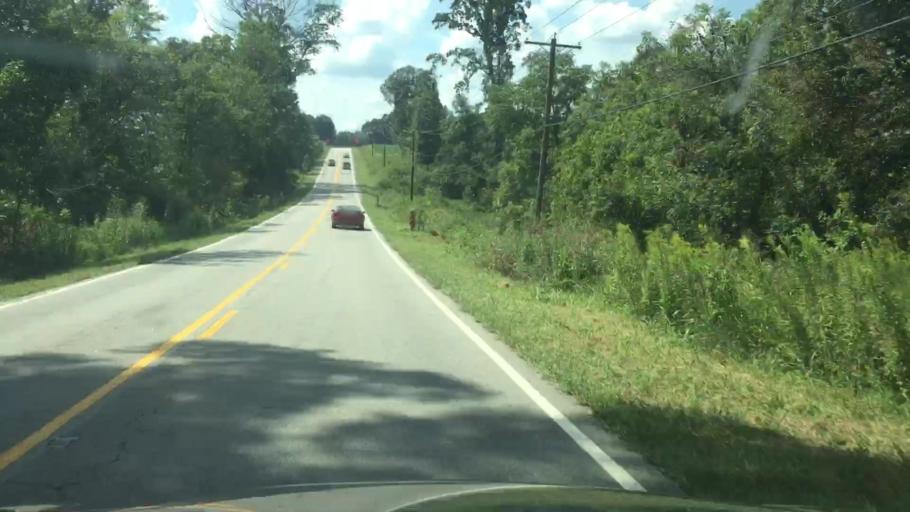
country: US
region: North Carolina
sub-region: Rowan County
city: China Grove
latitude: 35.6494
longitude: -80.6172
